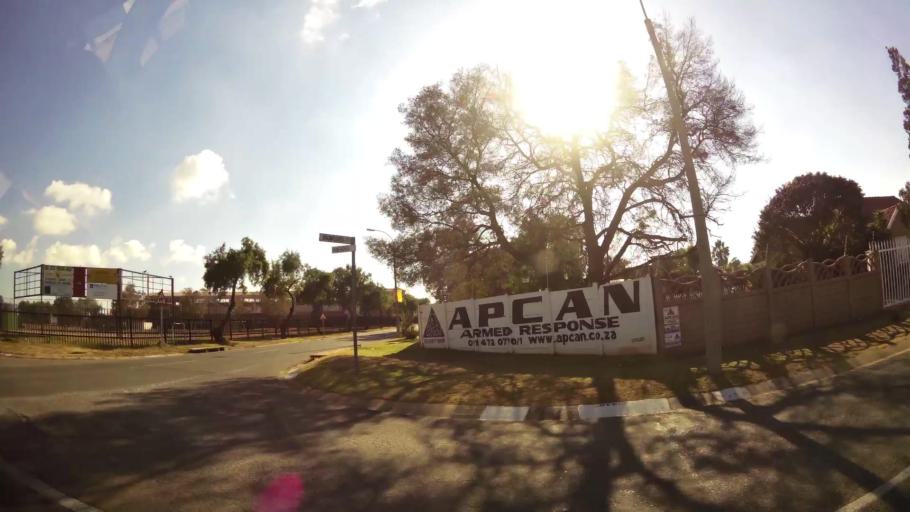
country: ZA
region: Gauteng
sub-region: City of Johannesburg Metropolitan Municipality
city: Roodepoort
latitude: -26.1562
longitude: 27.8283
